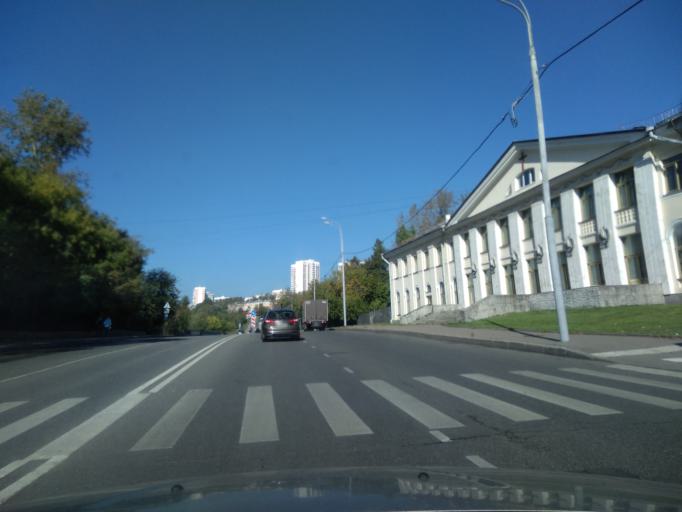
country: RU
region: Moscow
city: Strogino
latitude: 55.8391
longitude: 37.4088
